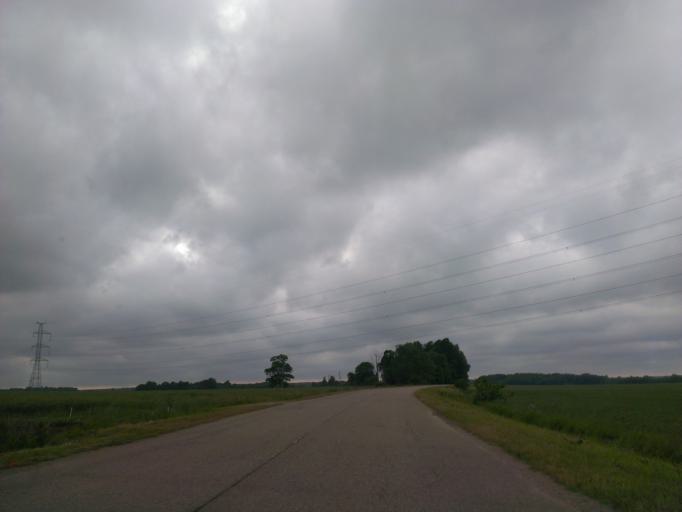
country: LV
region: Aizpute
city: Aizpute
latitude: 56.7226
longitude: 21.4366
